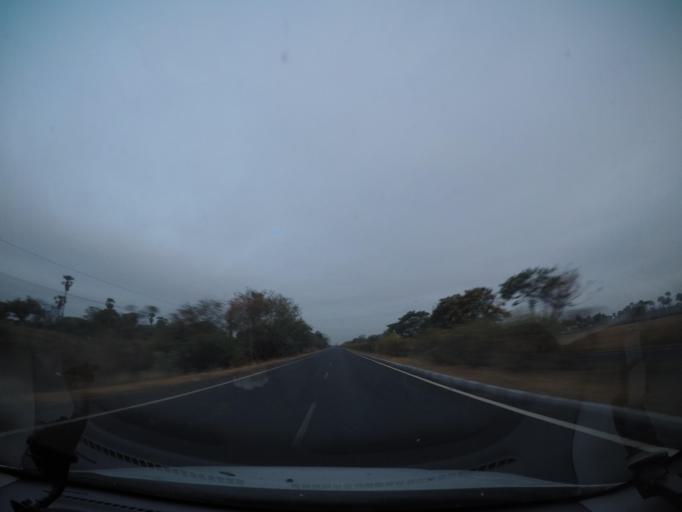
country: IN
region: Andhra Pradesh
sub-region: West Godavari
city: Tadepallegudem
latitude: 16.8102
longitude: 81.3414
